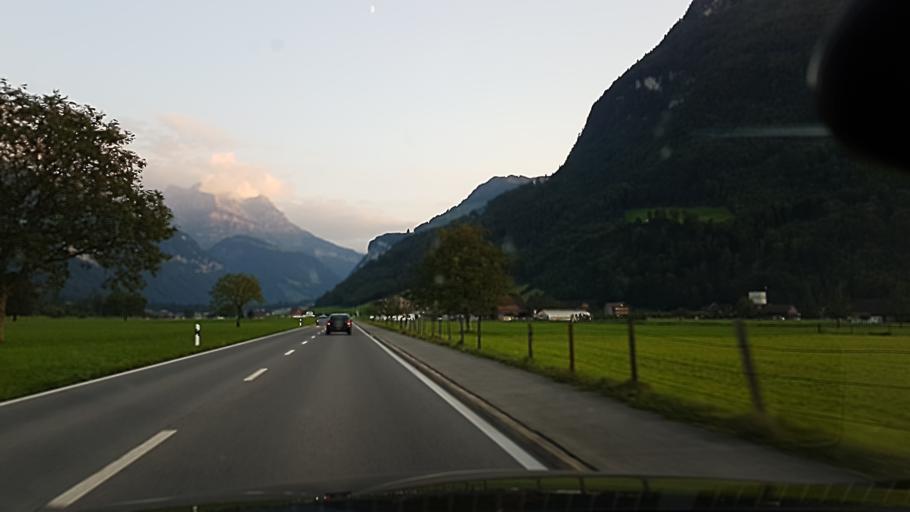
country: CH
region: Nidwalden
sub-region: Nidwalden
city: Stans
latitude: 46.9527
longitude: 8.3876
